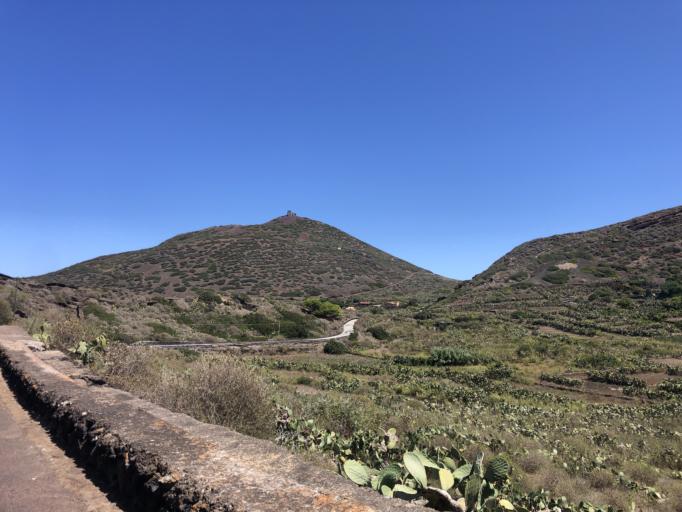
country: IT
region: Sicily
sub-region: Agrigento
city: Lampedusa
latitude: 35.8619
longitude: 12.8659
